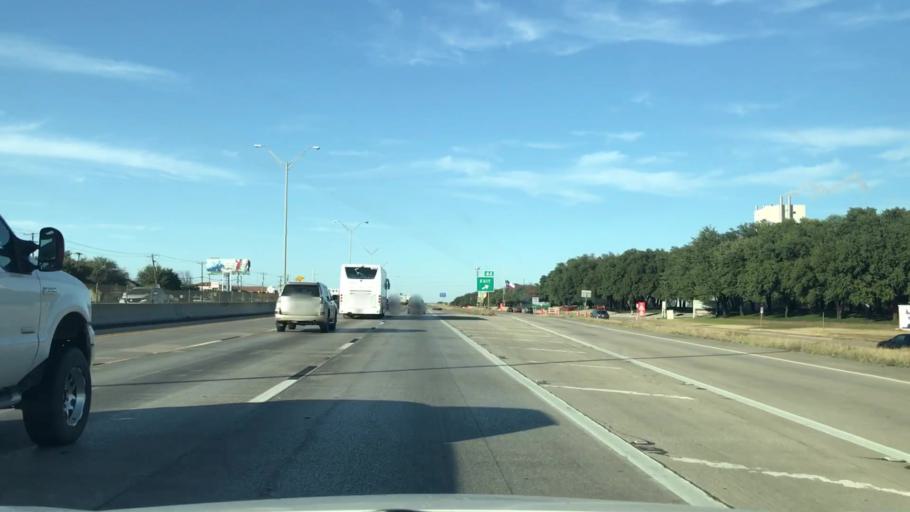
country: US
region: Texas
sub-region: Tarrant County
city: Edgecliff Village
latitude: 32.6390
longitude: -97.3215
